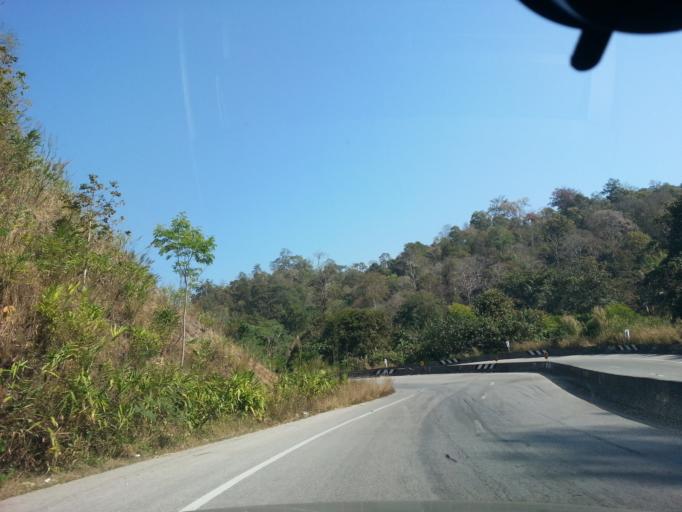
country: TH
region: Chiang Mai
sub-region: Amphoe Chiang Dao
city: Chiang Dao
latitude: 19.2451
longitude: 98.9689
